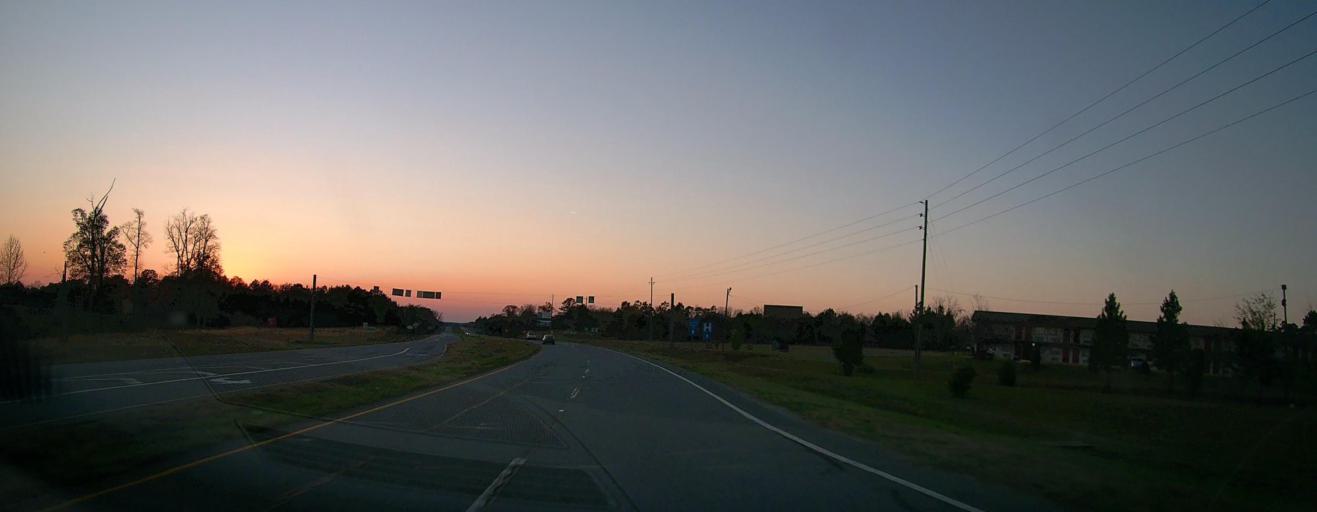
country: US
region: Georgia
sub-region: Dodge County
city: Eastman
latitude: 32.1749
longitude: -83.1617
